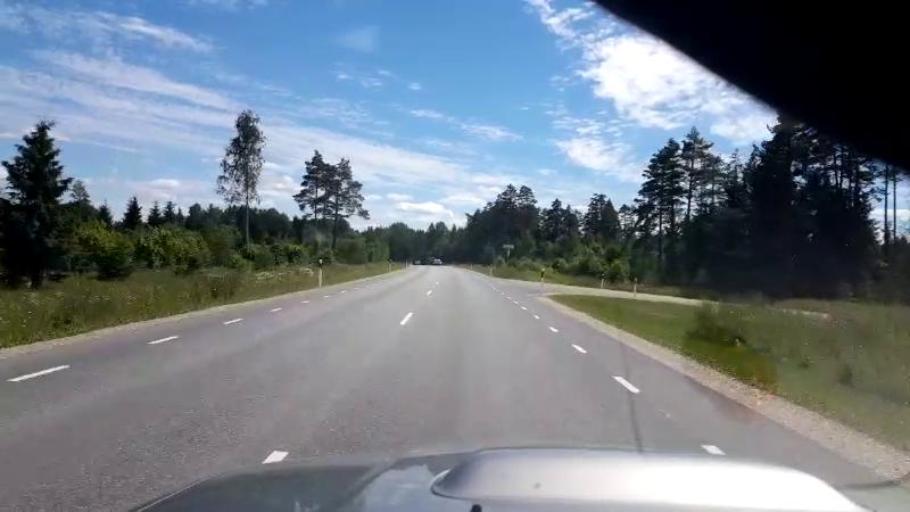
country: EE
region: Jogevamaa
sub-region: Jogeva linn
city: Jogeva
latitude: 58.7909
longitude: 26.3107
